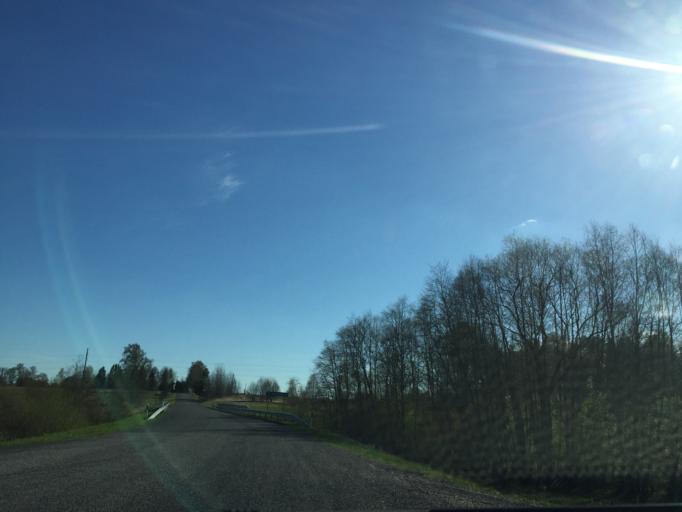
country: EE
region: Valgamaa
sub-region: Valga linn
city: Valga
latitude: 57.8386
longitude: 26.2358
